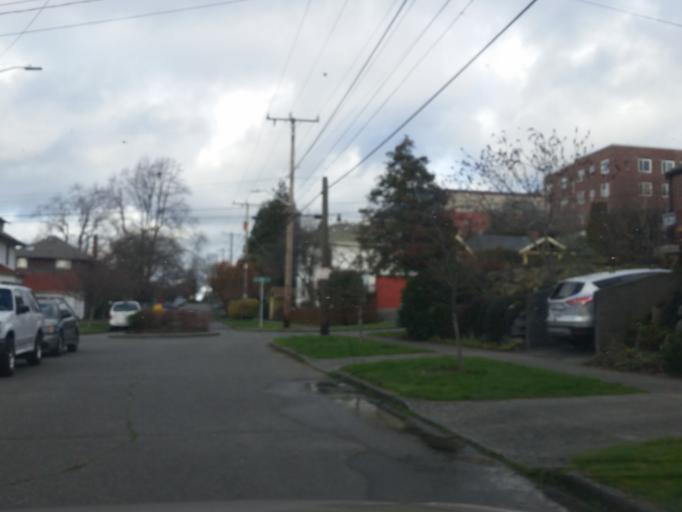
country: US
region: Washington
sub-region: King County
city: Seattle
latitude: 47.6640
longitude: -122.3554
